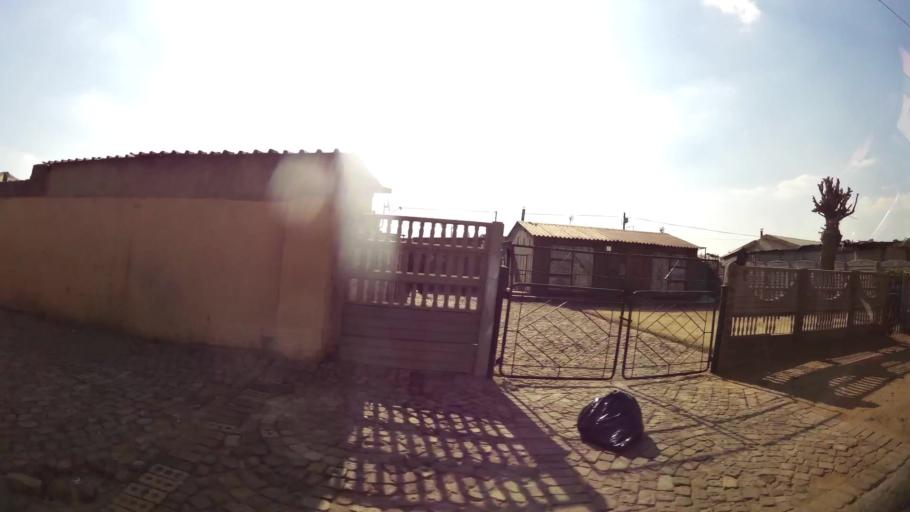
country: ZA
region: Gauteng
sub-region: Ekurhuleni Metropolitan Municipality
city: Brakpan
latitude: -26.1576
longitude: 28.4063
